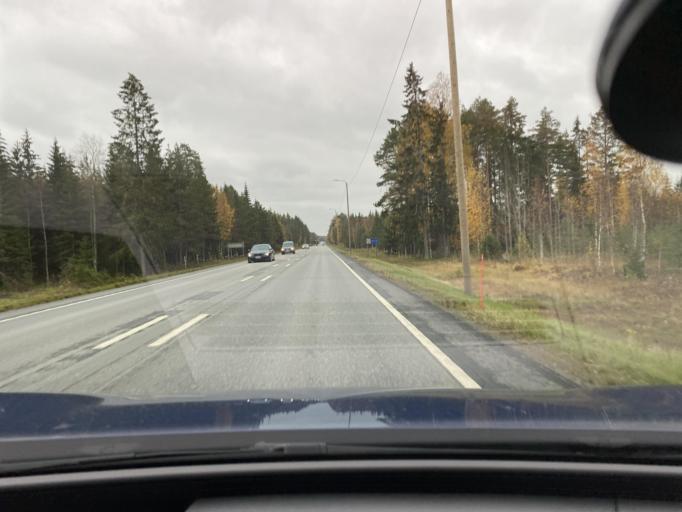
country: FI
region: Varsinais-Suomi
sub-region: Vakka-Suomi
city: Laitila
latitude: 60.9528
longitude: 21.5976
